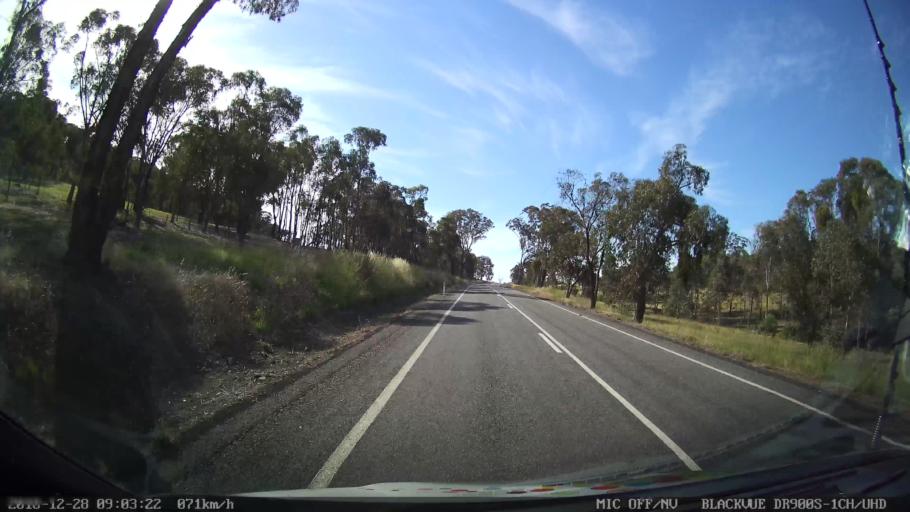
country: AU
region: New South Wales
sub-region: Upper Lachlan Shire
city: Crookwell
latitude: -34.1628
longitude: 149.3370
